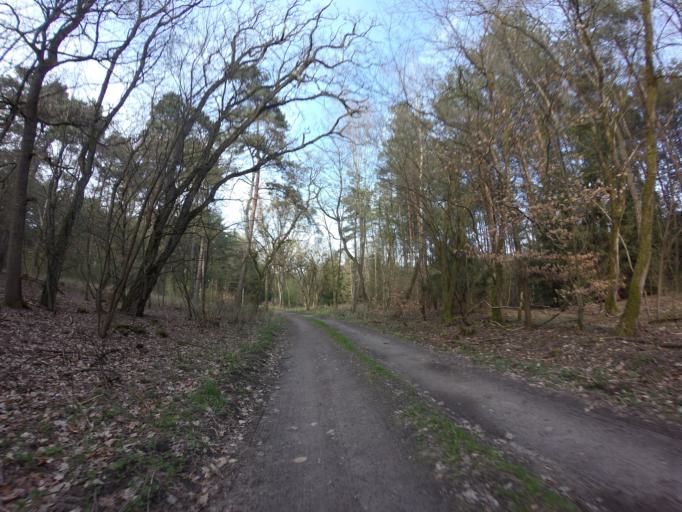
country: PL
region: West Pomeranian Voivodeship
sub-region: Powiat choszczenski
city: Recz
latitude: 53.1990
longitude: 15.5256
